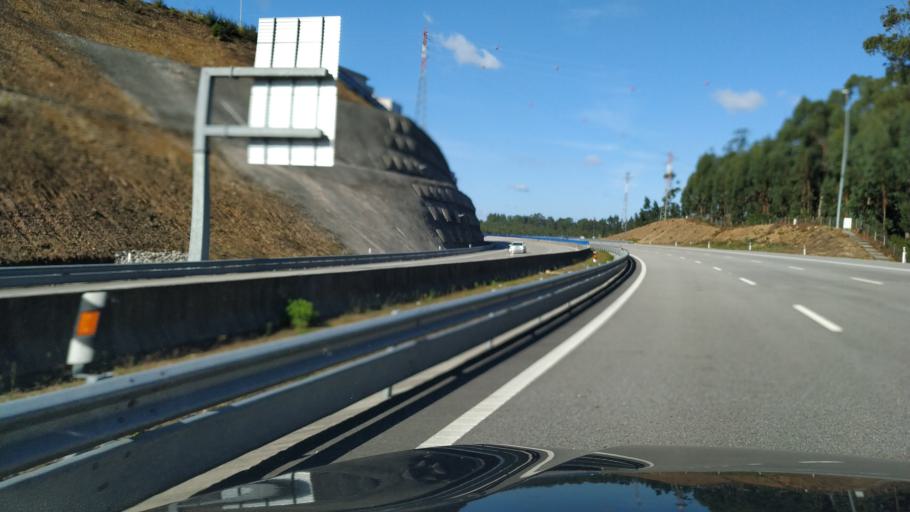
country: PT
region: Porto
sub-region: Vila Nova de Gaia
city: Olival
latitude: 41.0773
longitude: -8.5394
